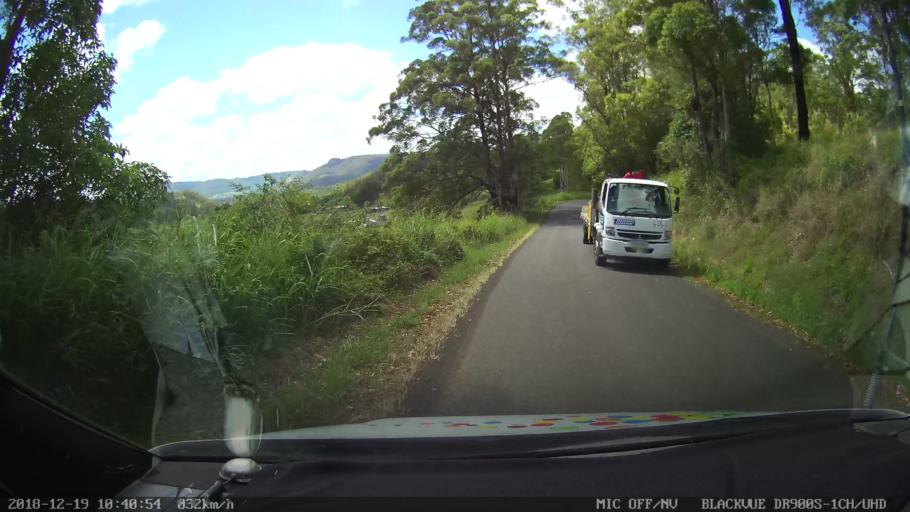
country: AU
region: New South Wales
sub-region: Lismore Municipality
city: Nimbin
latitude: -28.5870
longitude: 153.1599
